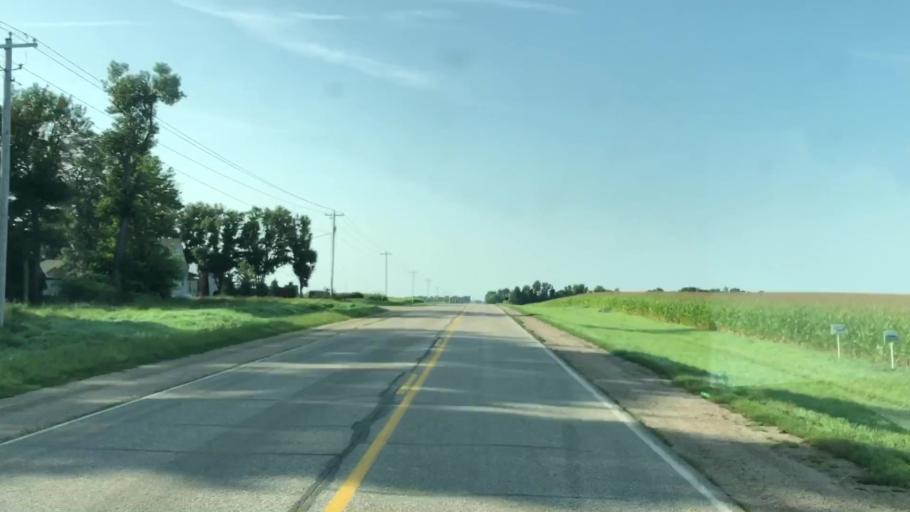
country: US
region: Iowa
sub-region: Lyon County
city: George
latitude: 43.3739
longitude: -95.9982
